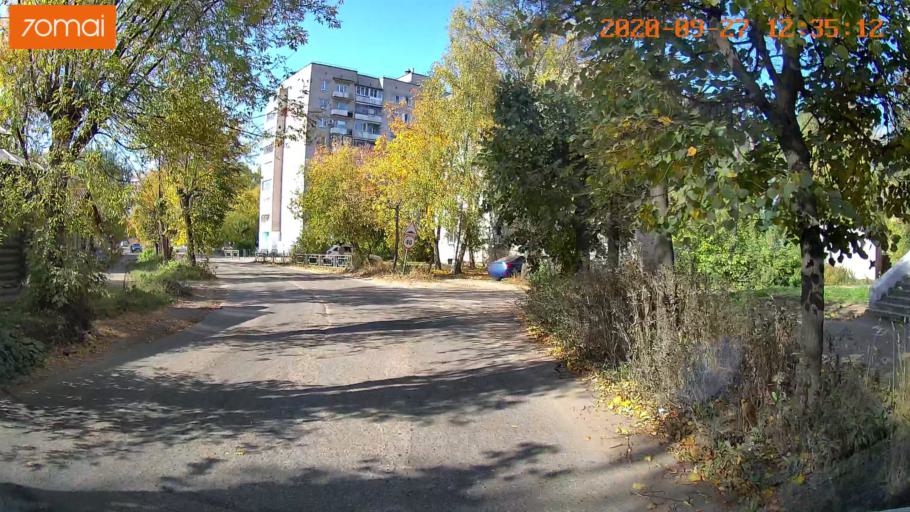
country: RU
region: Ivanovo
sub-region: Gorod Ivanovo
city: Ivanovo
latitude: 57.0187
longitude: 40.9724
